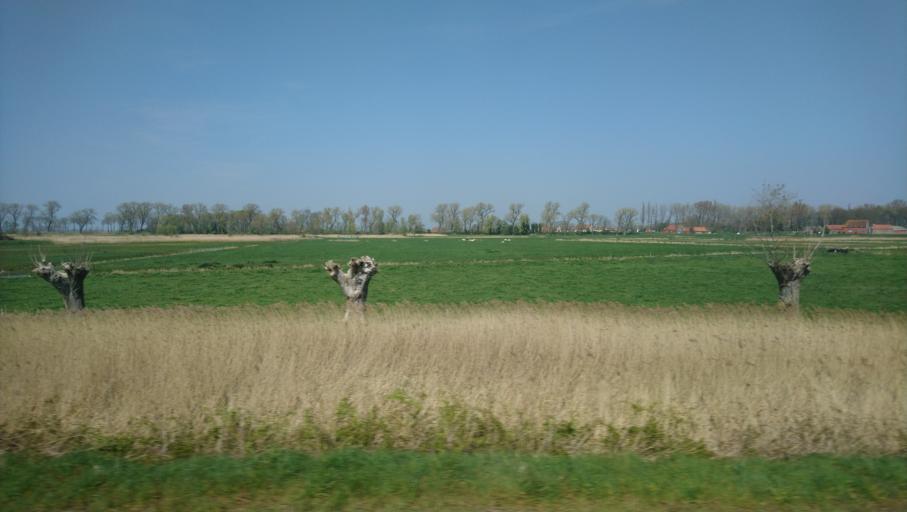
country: BE
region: Flanders
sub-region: Provincie West-Vlaanderen
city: Jabbeke
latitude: 51.2035
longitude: 3.1247
